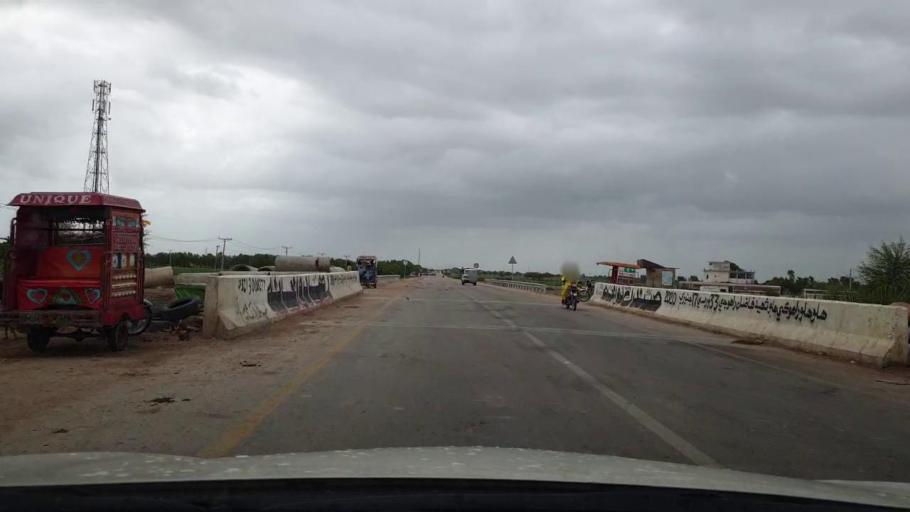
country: PK
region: Sindh
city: Badin
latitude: 24.6554
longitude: 68.7297
